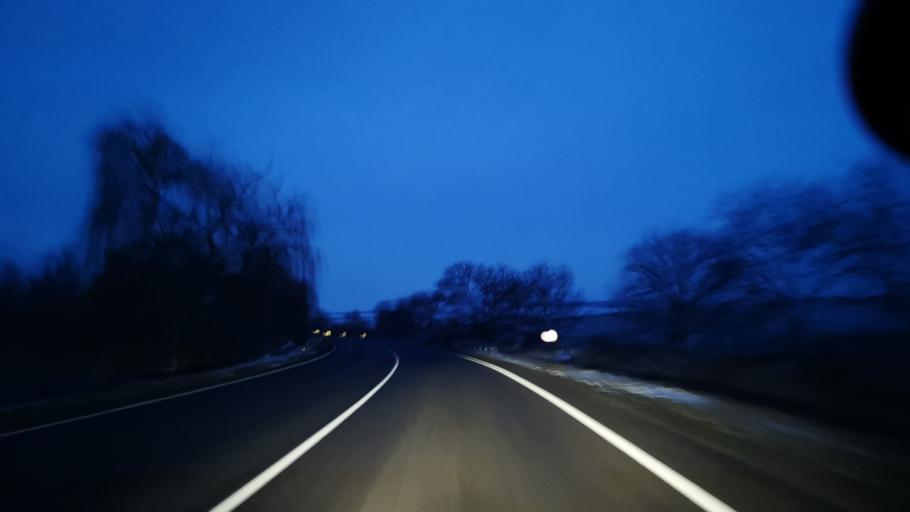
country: MD
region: Orhei
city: Orhei
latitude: 47.5039
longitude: 28.7971
